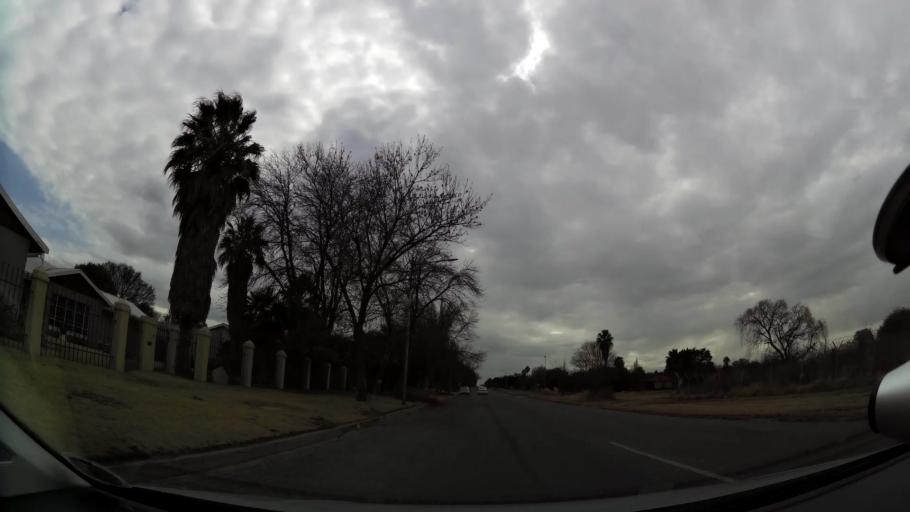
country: ZA
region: Orange Free State
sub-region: Fezile Dabi District Municipality
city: Kroonstad
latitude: -27.6401
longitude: 27.2386
